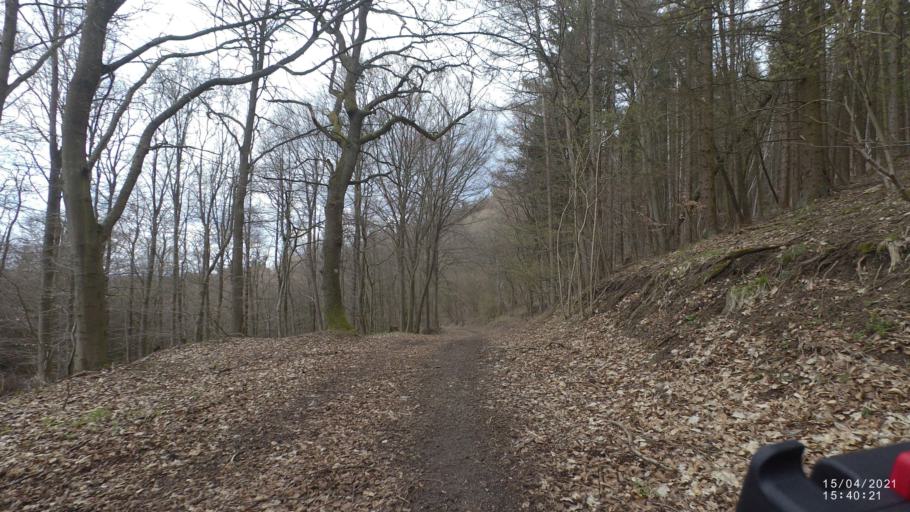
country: DE
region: Rheinland-Pfalz
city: Rieden
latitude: 50.3948
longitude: 7.2047
